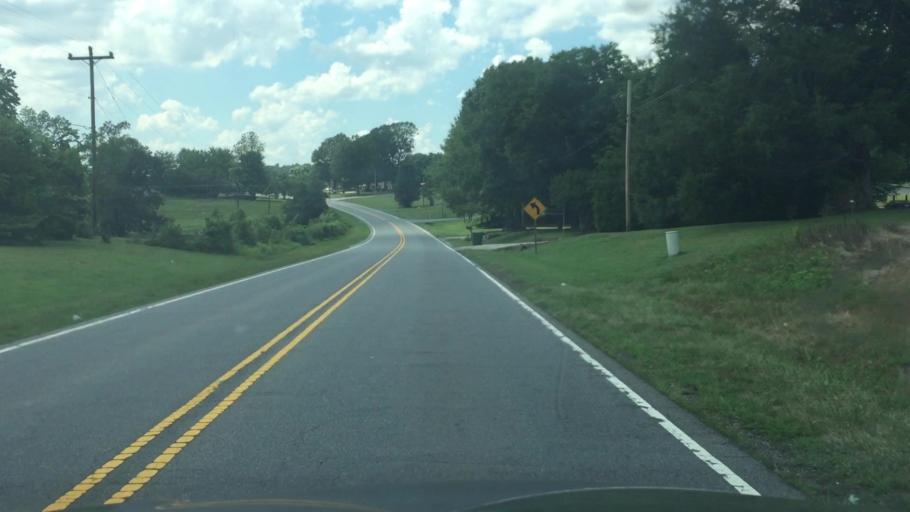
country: US
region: North Carolina
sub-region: Rowan County
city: Enochville
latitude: 35.5733
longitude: -80.6580
